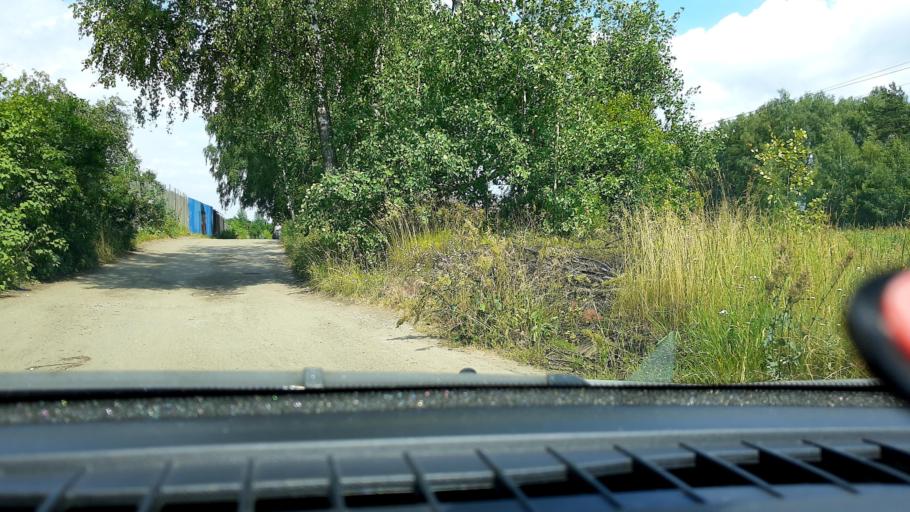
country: RU
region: Nizjnij Novgorod
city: Neklyudovo
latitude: 56.4479
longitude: 44.0039
